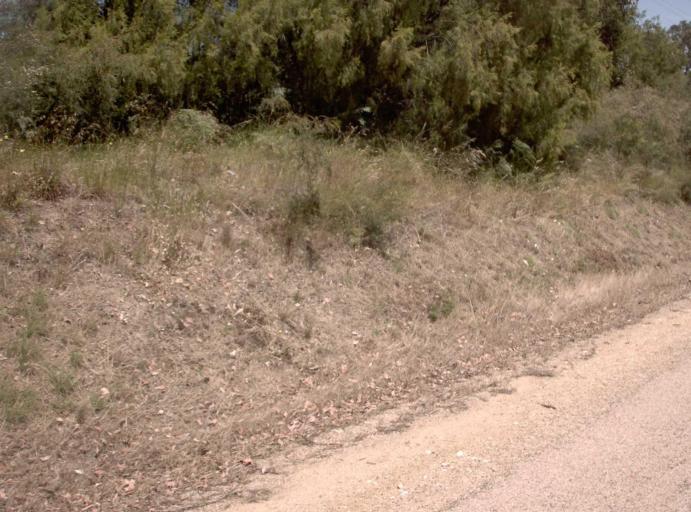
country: AU
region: Victoria
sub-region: East Gippsland
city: Bairnsdale
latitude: -37.7515
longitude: 147.7451
